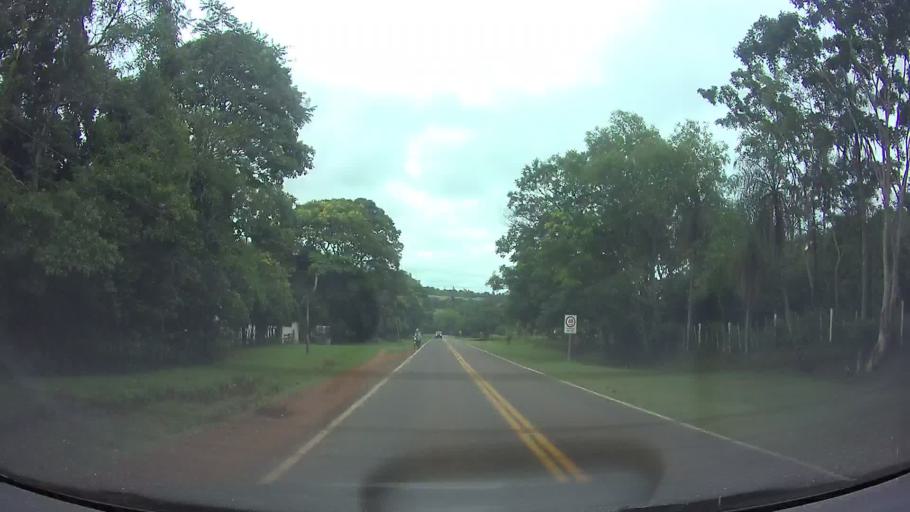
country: PY
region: Paraguari
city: Acahay
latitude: -25.9331
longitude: -57.1052
